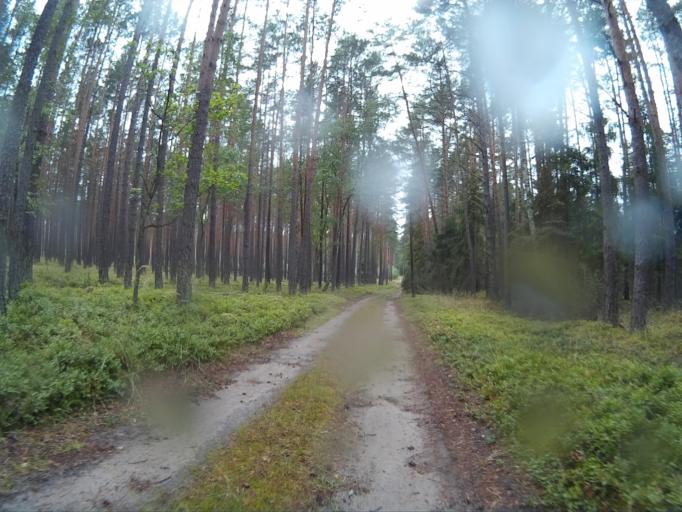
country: PL
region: Kujawsko-Pomorskie
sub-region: Powiat swiecki
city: Osie
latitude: 53.6586
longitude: 18.3824
